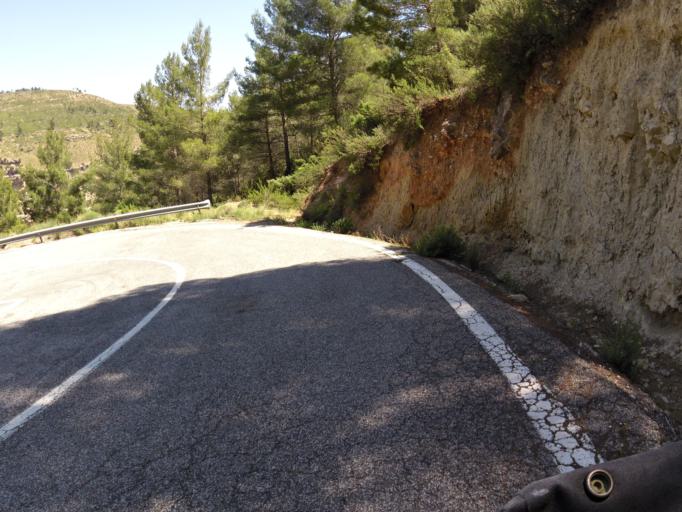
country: ES
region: Valencia
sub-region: Provincia de Valencia
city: Casas Bajas
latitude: 39.9837
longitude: -1.2760
